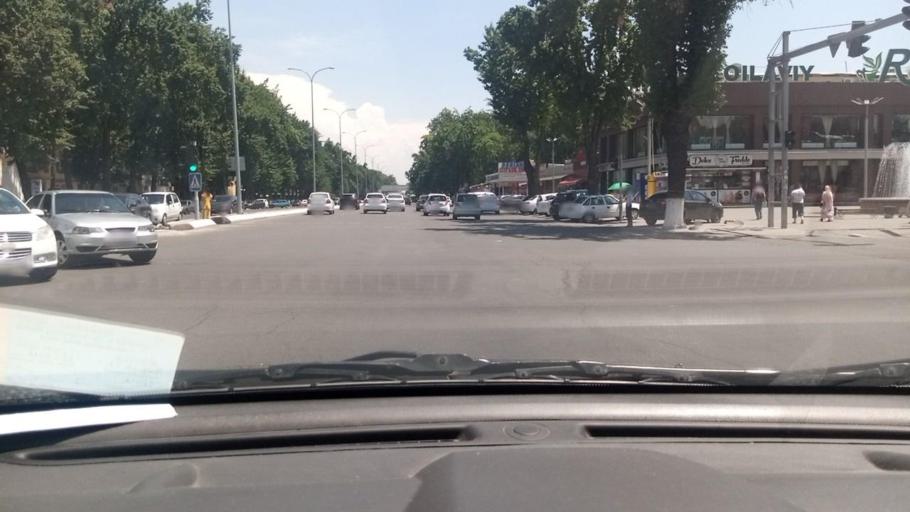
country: UZ
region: Toshkent Shahri
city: Tashkent
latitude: 41.2866
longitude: 69.2053
